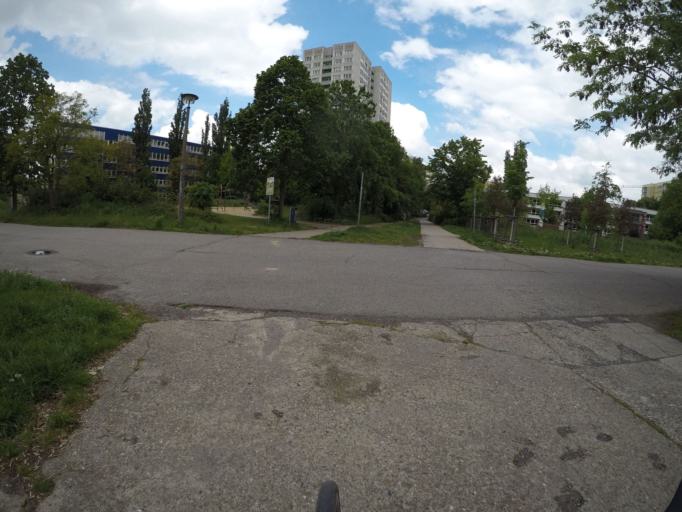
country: DE
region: Berlin
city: Marzahn
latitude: 52.5521
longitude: 13.5573
